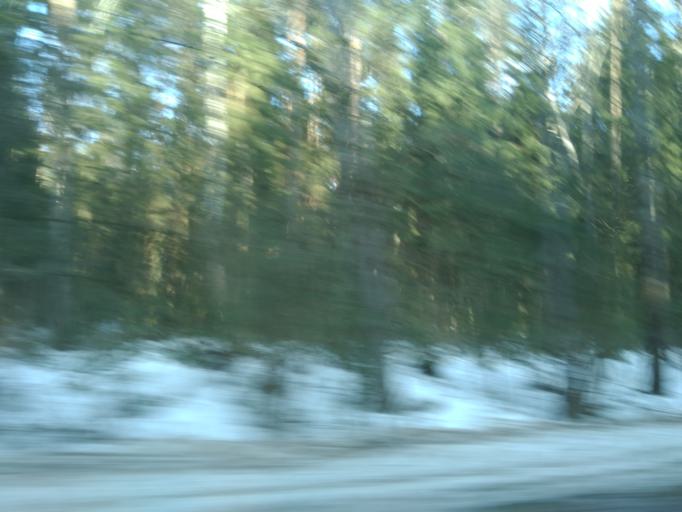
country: BY
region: Minsk
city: Snow
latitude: 53.2667
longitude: 26.3592
